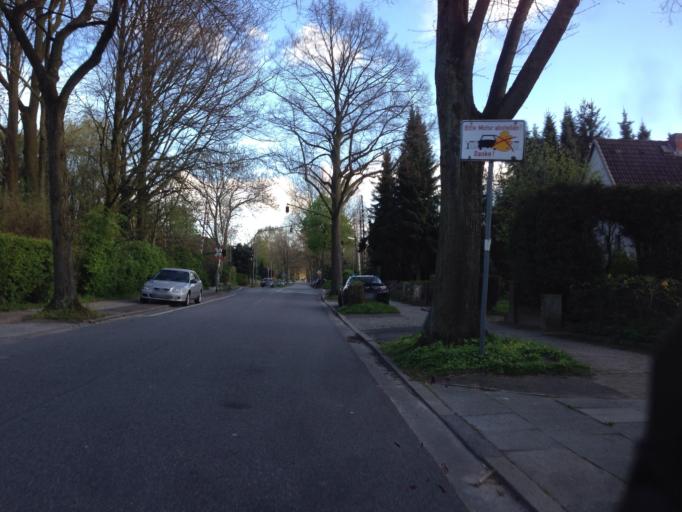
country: DE
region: Hamburg
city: Marienthal
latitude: 53.5685
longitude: 10.0685
